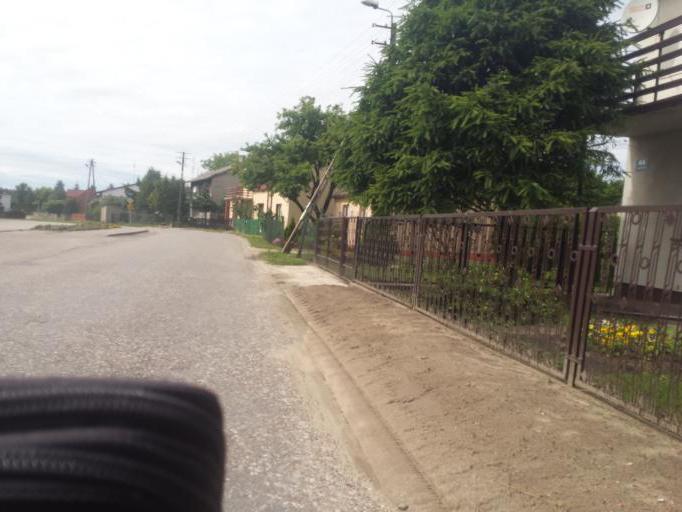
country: PL
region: Warmian-Masurian Voivodeship
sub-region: Powiat ilawski
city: Ilawa
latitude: 53.5281
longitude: 19.5054
